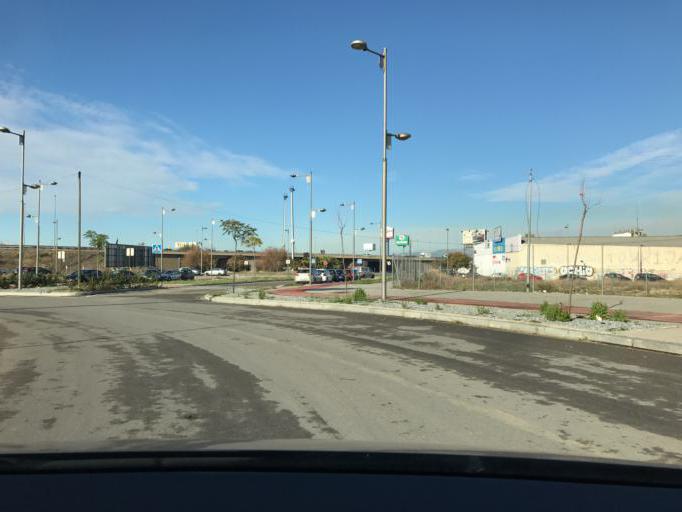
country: ES
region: Andalusia
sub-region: Provincia de Granada
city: Armilla
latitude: 37.1523
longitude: -3.6106
